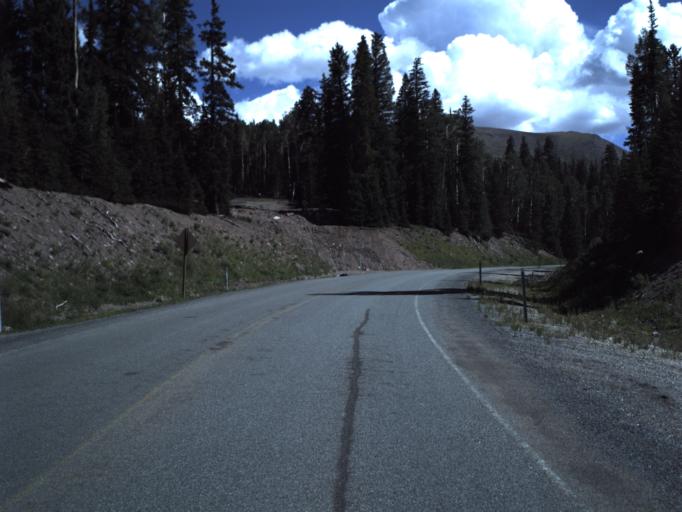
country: US
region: Utah
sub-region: Piute County
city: Junction
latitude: 38.3249
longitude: -112.3749
